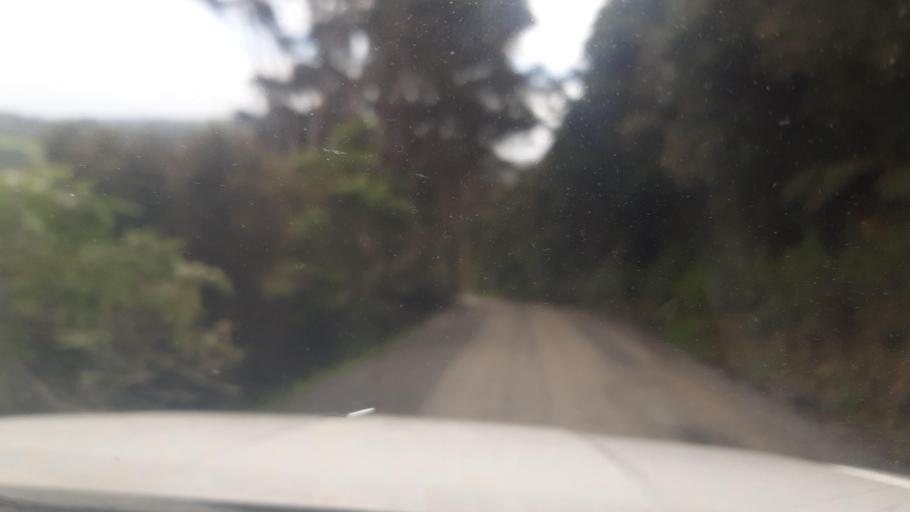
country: NZ
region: Northland
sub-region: Far North District
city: Taipa
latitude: -35.0739
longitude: 173.5234
